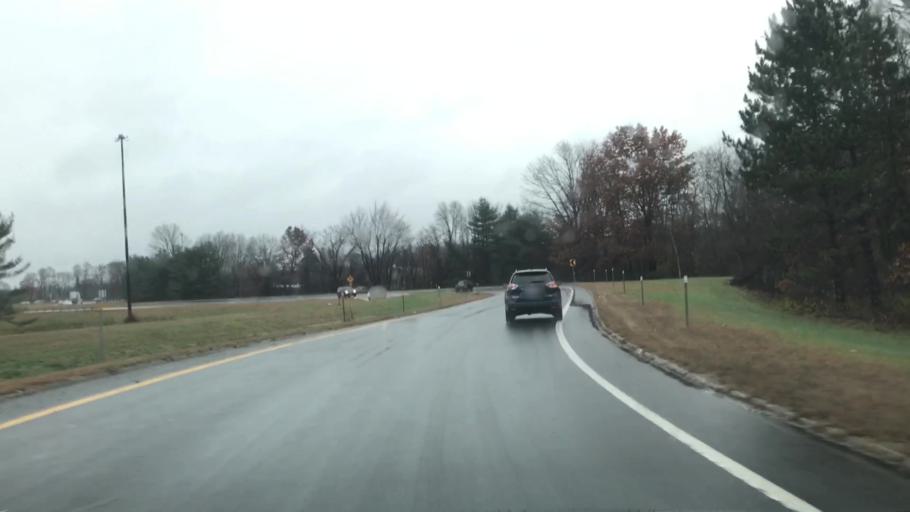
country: US
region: New Hampshire
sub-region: Merrimack County
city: Concord
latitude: 43.2147
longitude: -71.5330
